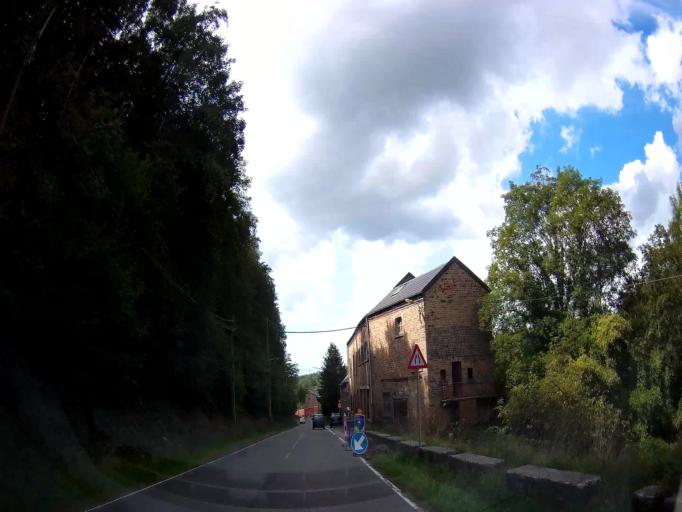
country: BE
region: Wallonia
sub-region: Province de Liege
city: Modave
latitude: 50.4509
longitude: 5.2885
